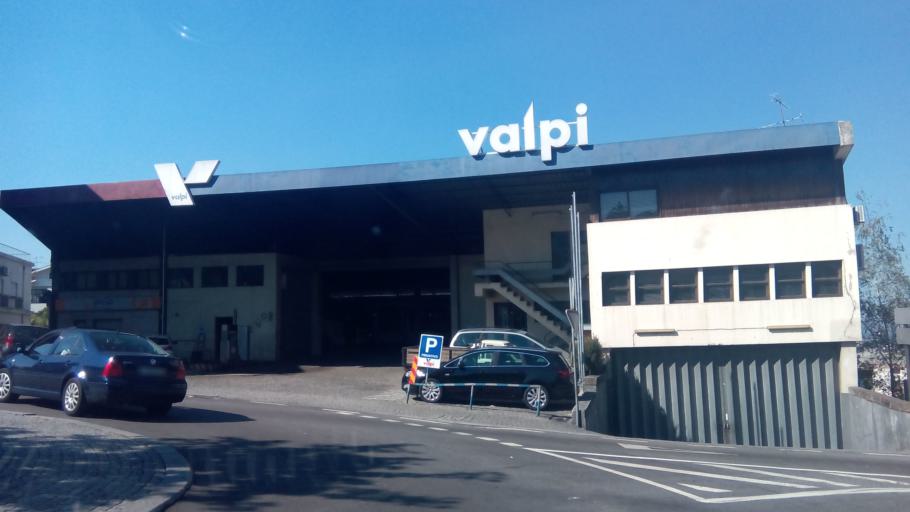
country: PT
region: Porto
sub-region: Penafiel
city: Penafiel
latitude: 41.2074
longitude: -8.2823
